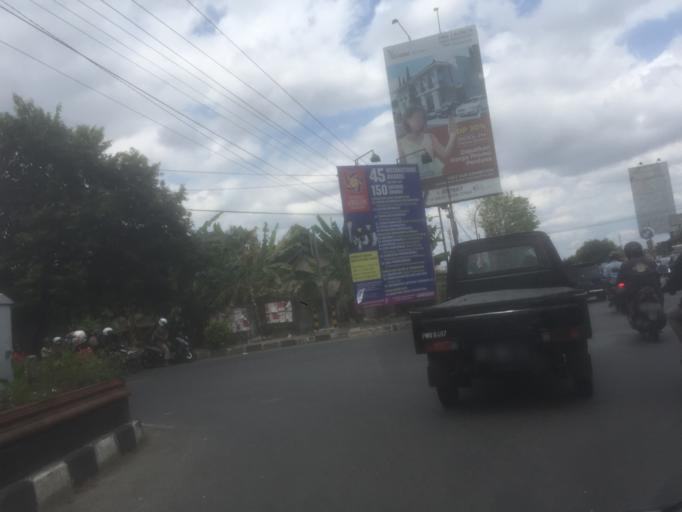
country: ID
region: Daerah Istimewa Yogyakarta
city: Sleman
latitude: -7.7215
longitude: 110.3614
